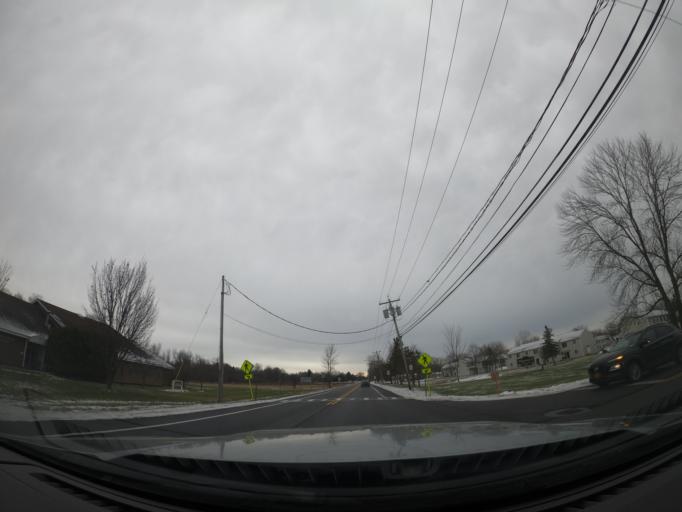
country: US
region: New York
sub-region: Madison County
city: Bridgeport
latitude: 43.1530
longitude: -75.9737
